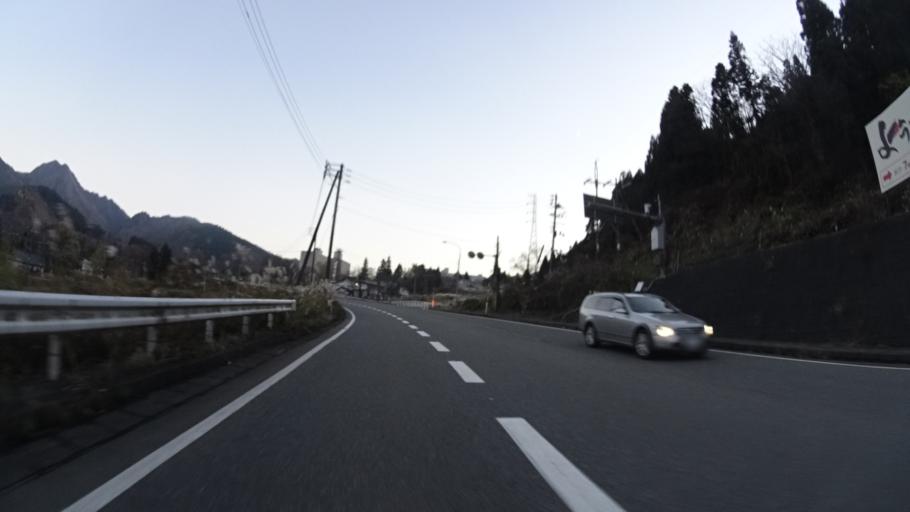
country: JP
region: Niigata
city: Shiozawa
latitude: 36.9732
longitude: 138.8002
